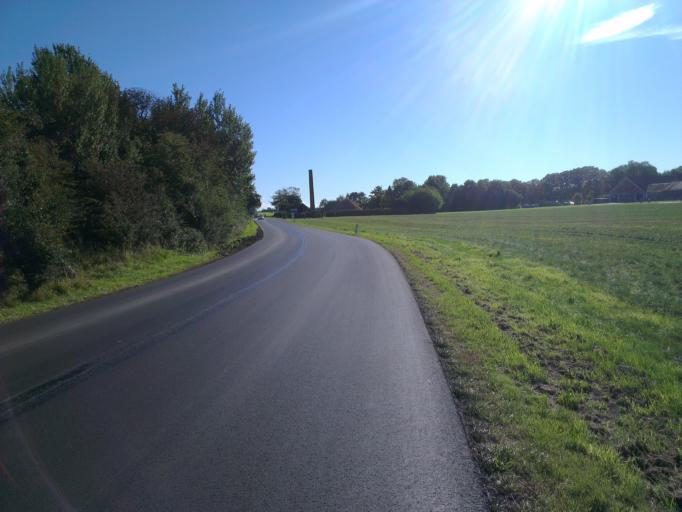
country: DK
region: Capital Region
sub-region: Frederikssund Kommune
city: Jaegerspris
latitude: 55.8575
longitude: 11.9723
